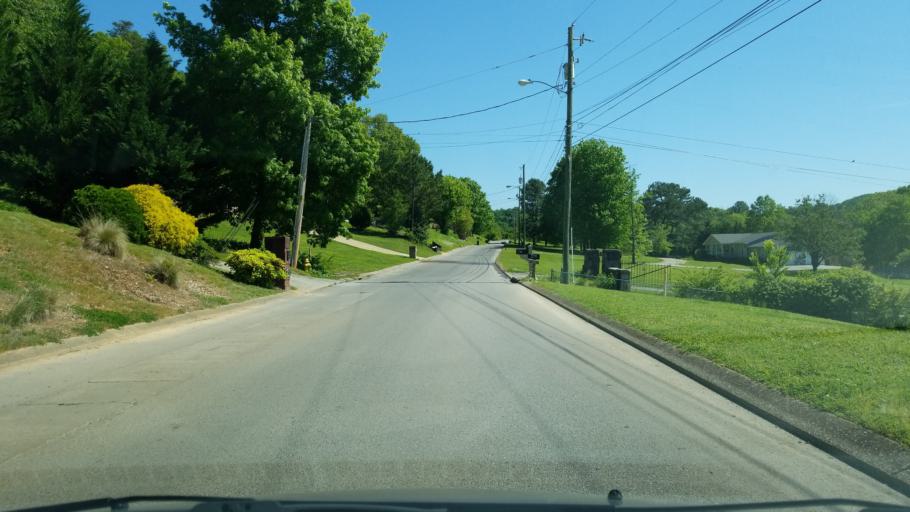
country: US
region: Tennessee
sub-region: Hamilton County
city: Red Bank
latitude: 35.1368
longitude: -85.3027
